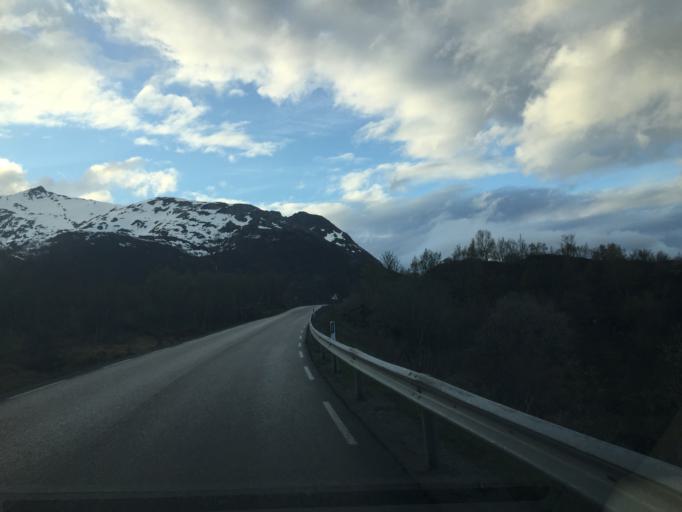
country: NO
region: Nordland
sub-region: Vagan
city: Svolvaer
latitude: 68.3206
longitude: 14.6994
